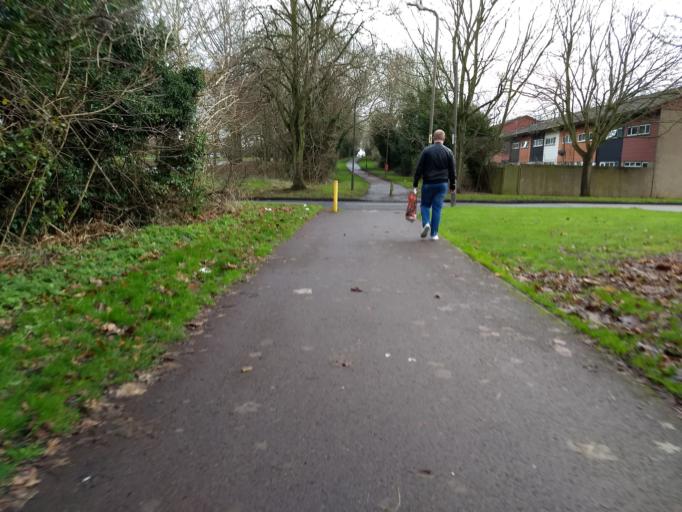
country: GB
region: England
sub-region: Buckinghamshire
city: Newton Longville
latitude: 51.9969
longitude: -0.7701
